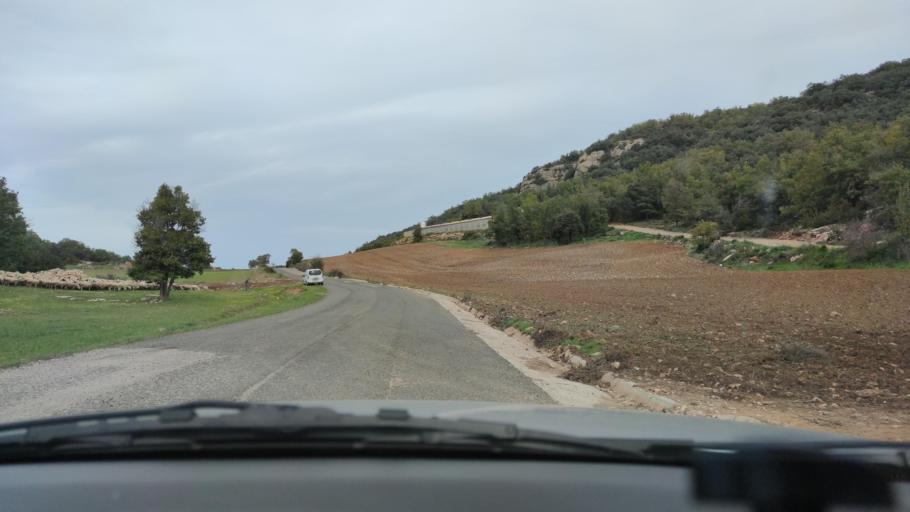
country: ES
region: Catalonia
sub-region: Provincia de Lleida
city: Llimiana
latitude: 42.0362
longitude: 1.0060
